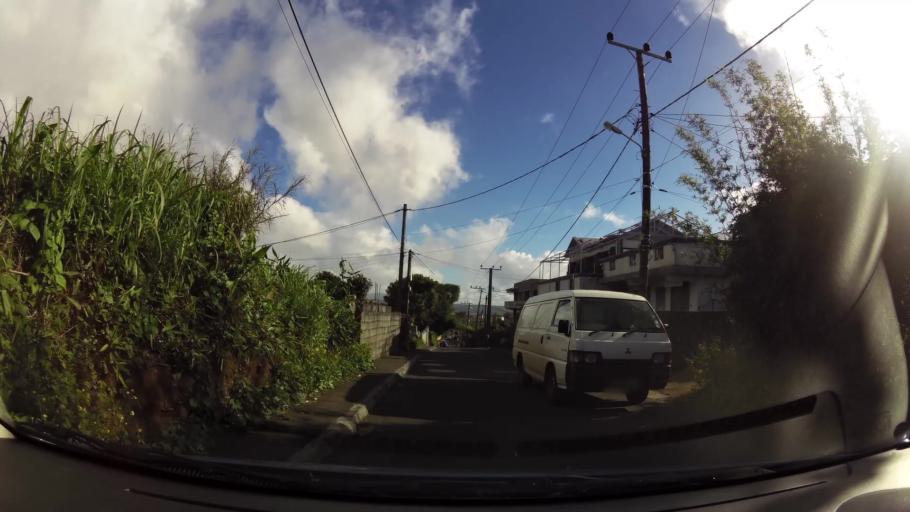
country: MU
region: Plaines Wilhems
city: Curepipe
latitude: -20.3243
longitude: 57.5082
